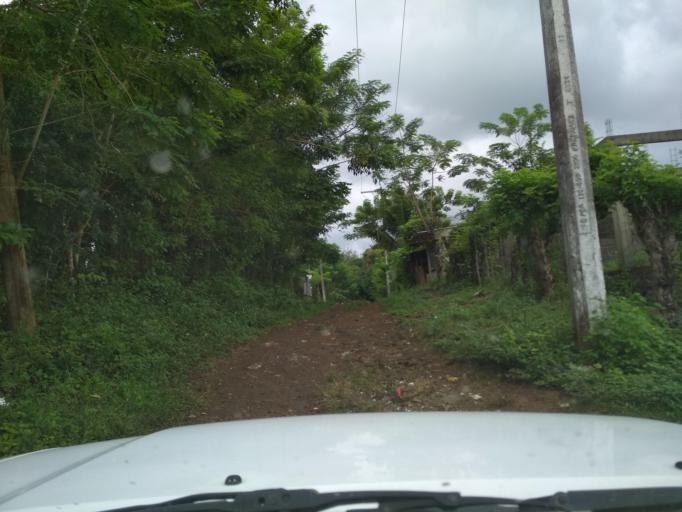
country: MX
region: Veracruz
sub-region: San Andres Tuxtla
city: Matacapan
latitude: 18.4256
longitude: -95.1793
